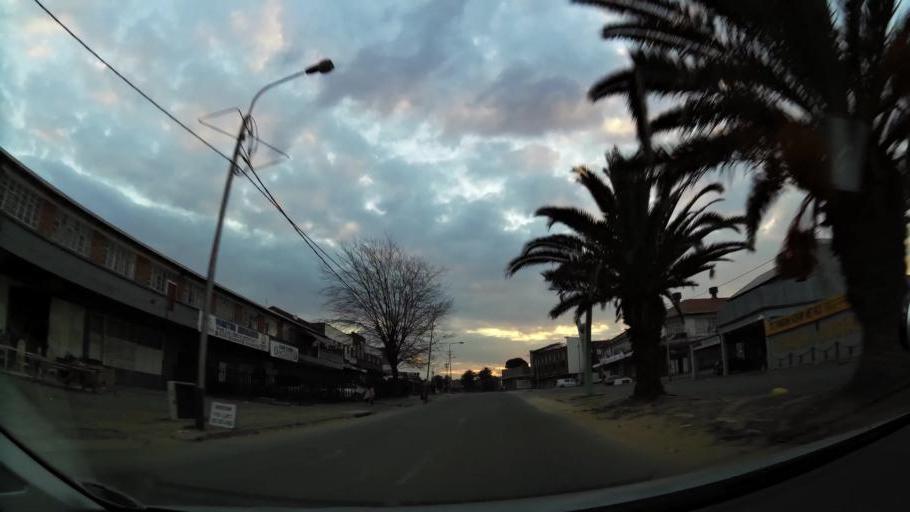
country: ZA
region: Gauteng
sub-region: Ekurhuleni Metropolitan Municipality
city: Germiston
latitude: -26.2020
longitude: 28.1225
